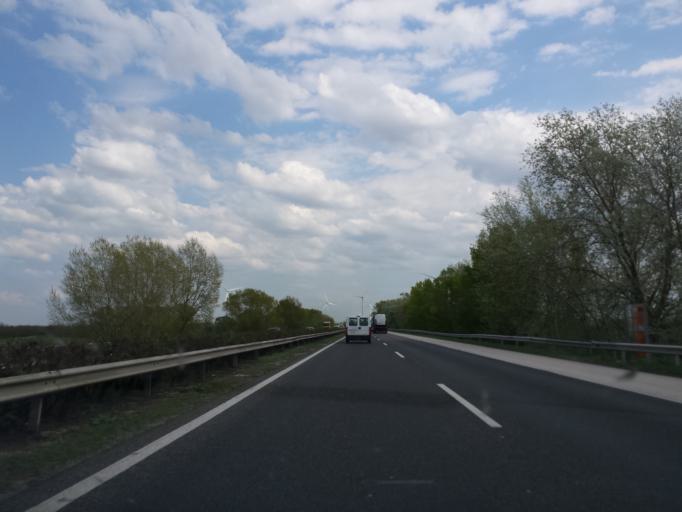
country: HU
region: Komarom-Esztergom
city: Acs
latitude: 47.6779
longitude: 18.0466
